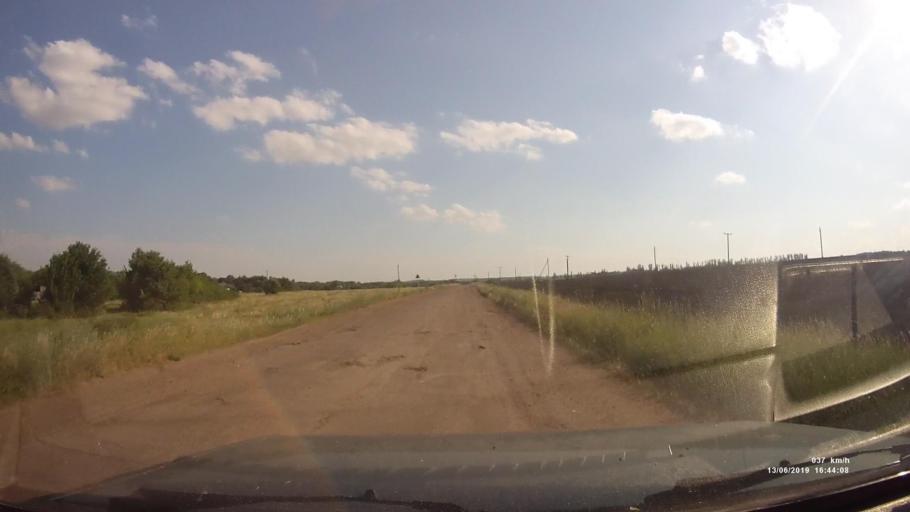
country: RU
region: Rostov
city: Kazanskaya
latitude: 49.9470
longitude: 41.4219
